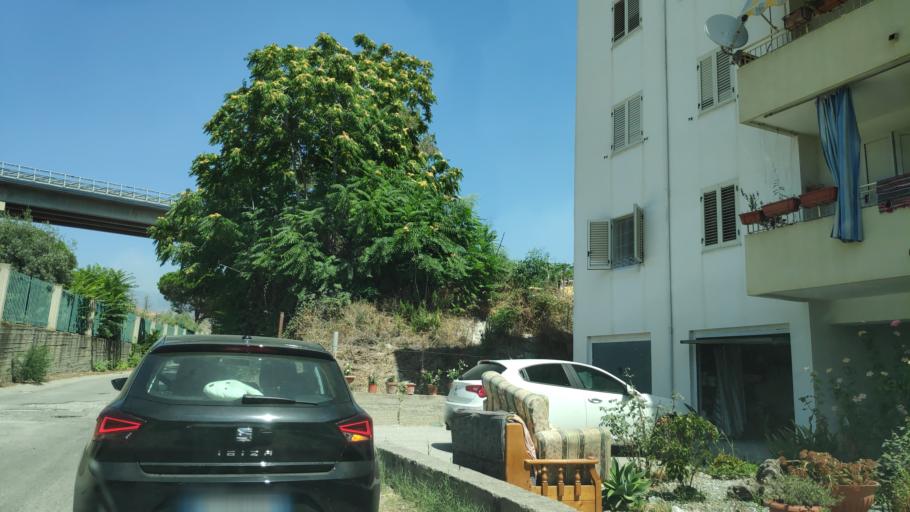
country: IT
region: Calabria
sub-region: Provincia di Reggio Calabria
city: Bova Marina
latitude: 37.9315
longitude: 15.9107
